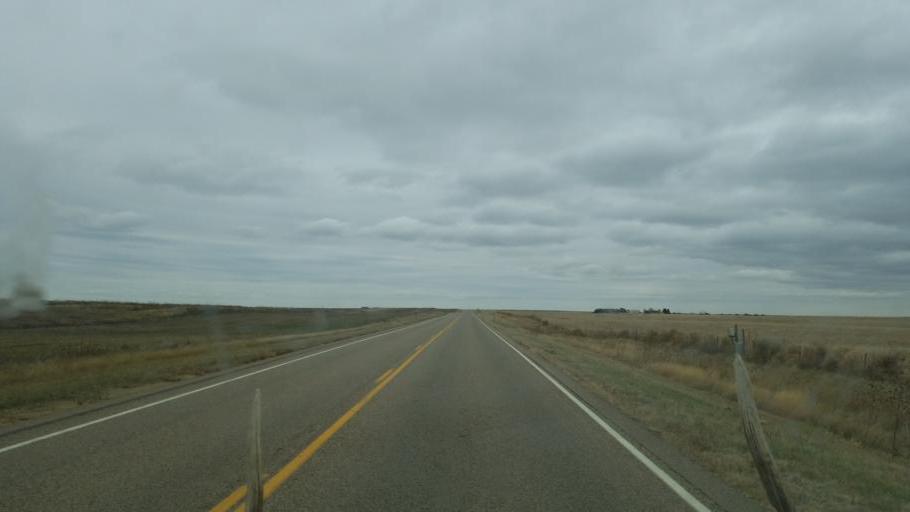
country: US
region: Colorado
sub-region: Cheyenne County
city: Cheyenne Wells
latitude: 38.8350
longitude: -102.2877
